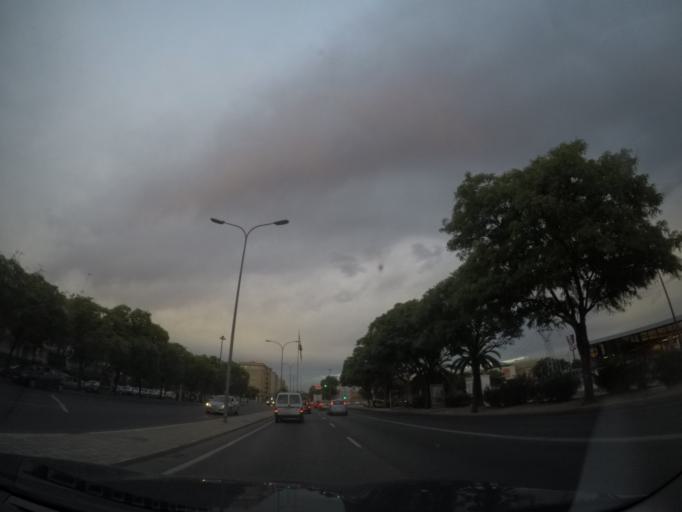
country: ES
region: Andalusia
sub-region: Provincia de Sevilla
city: Sevilla
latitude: 37.3873
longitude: -5.9574
